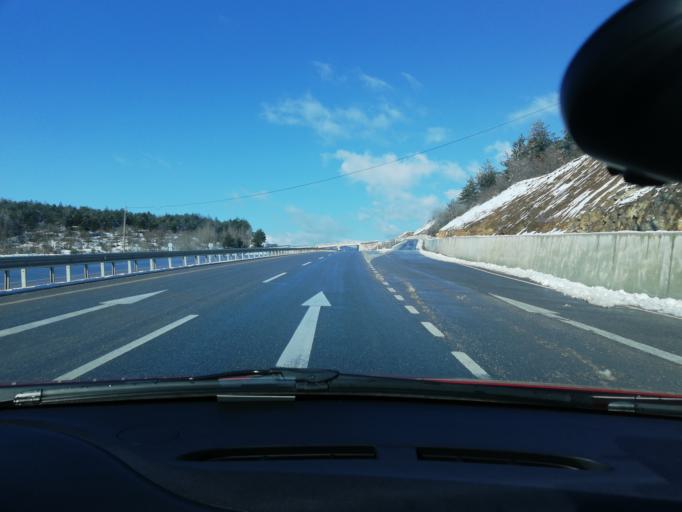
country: TR
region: Kastamonu
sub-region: Cide
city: Kastamonu
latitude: 41.3599
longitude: 33.6883
